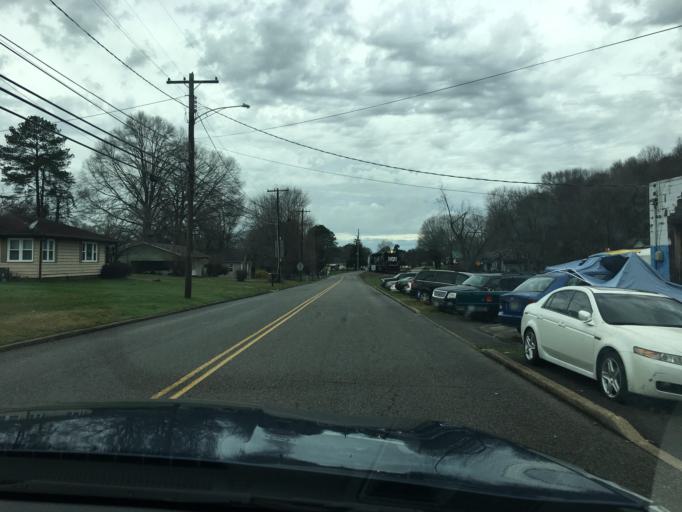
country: US
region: Tennessee
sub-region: McMinn County
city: Athens
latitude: 35.4584
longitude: -84.6057
